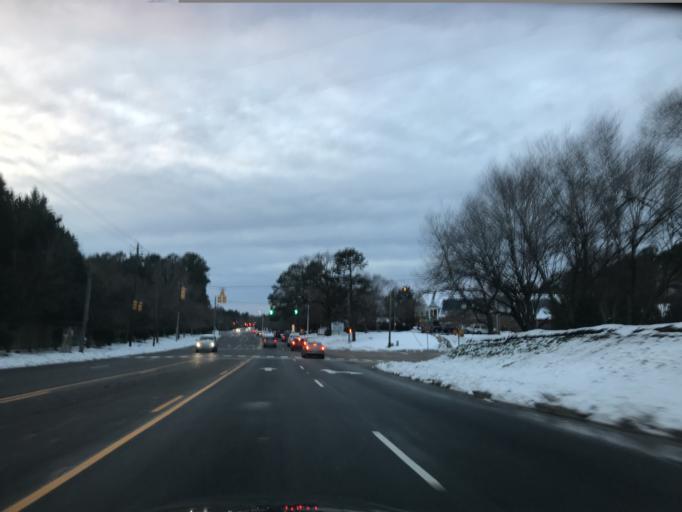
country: US
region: North Carolina
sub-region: Wake County
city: Wake Forest
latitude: 35.9034
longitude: -78.5838
